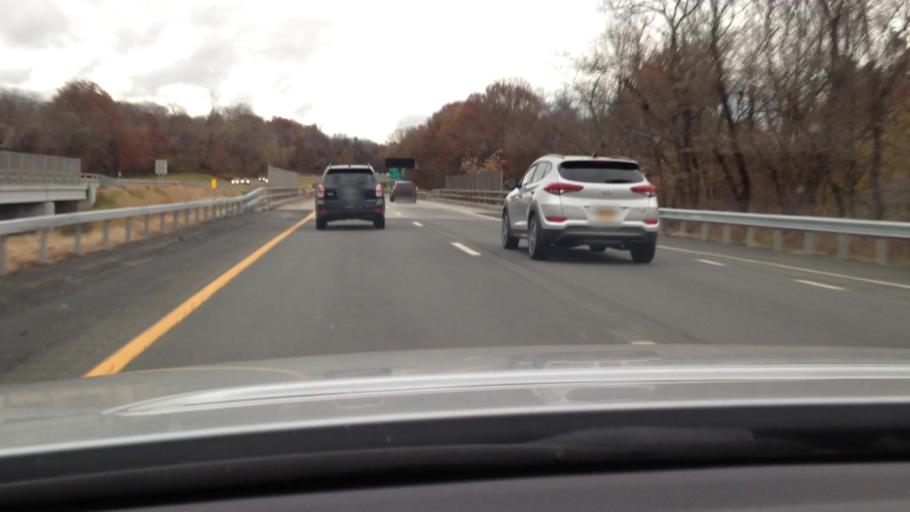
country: US
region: New York
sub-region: Rockland County
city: Chestnut Ridge
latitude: 41.0756
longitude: -74.0509
